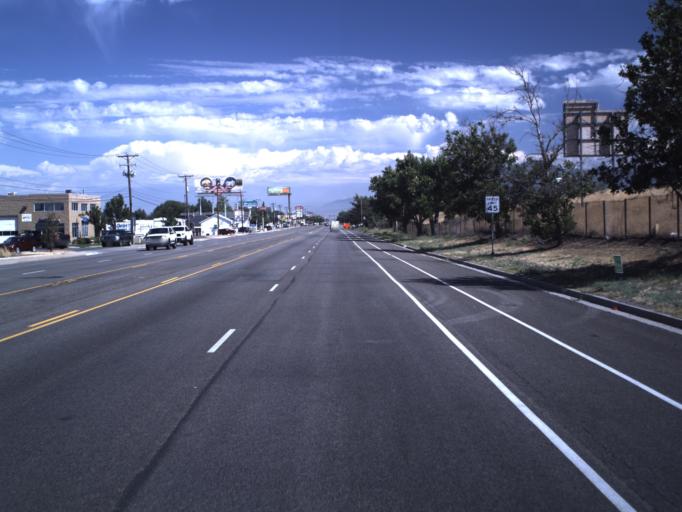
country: US
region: Utah
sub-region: Davis County
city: Sunset
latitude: 41.1406
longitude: -112.0260
